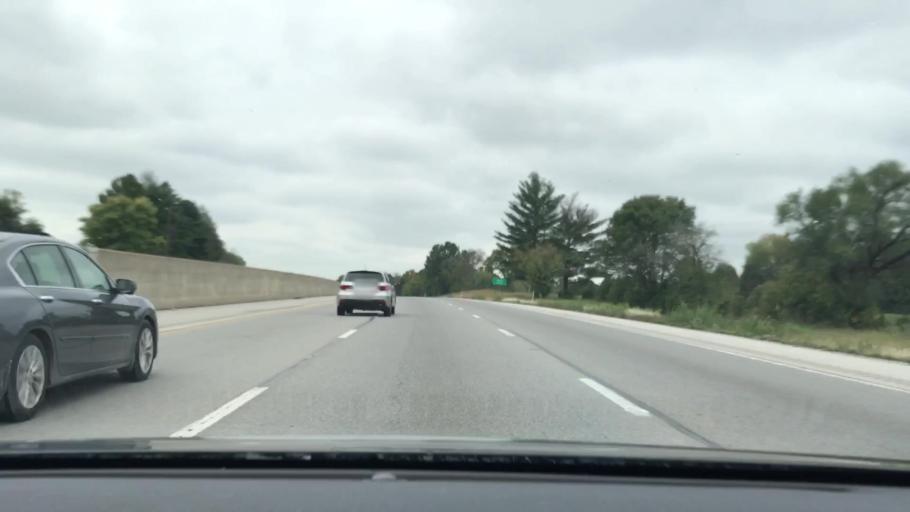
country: US
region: Kentucky
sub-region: Warren County
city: Plano
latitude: 36.8180
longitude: -86.4727
